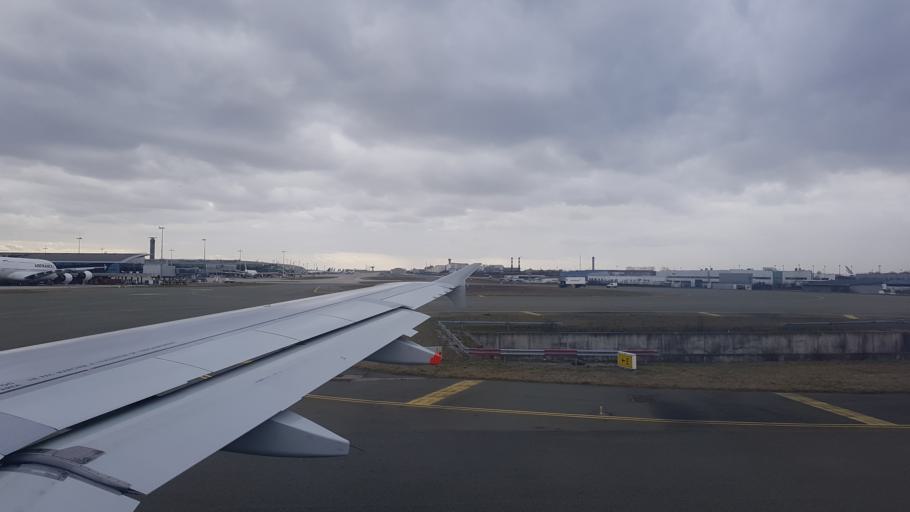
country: FR
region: Ile-de-France
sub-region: Departement de Seine-et-Marne
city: Mitry-Mory
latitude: 49.0093
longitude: 2.5953
